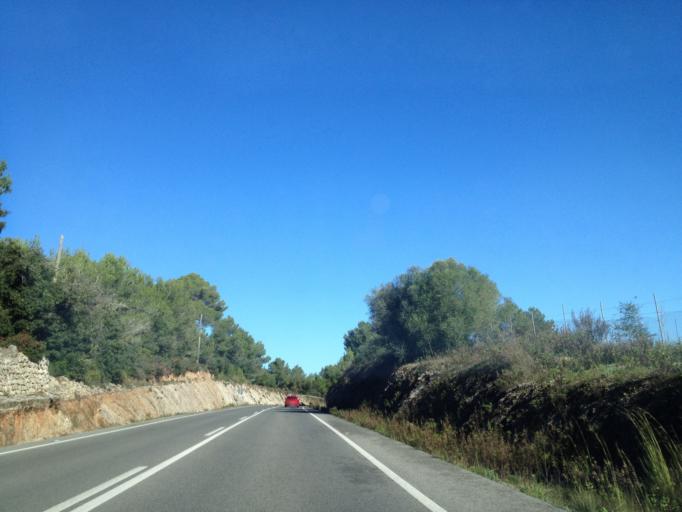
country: ES
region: Balearic Islands
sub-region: Illes Balears
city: Arta
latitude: 39.6615
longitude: 3.3187
